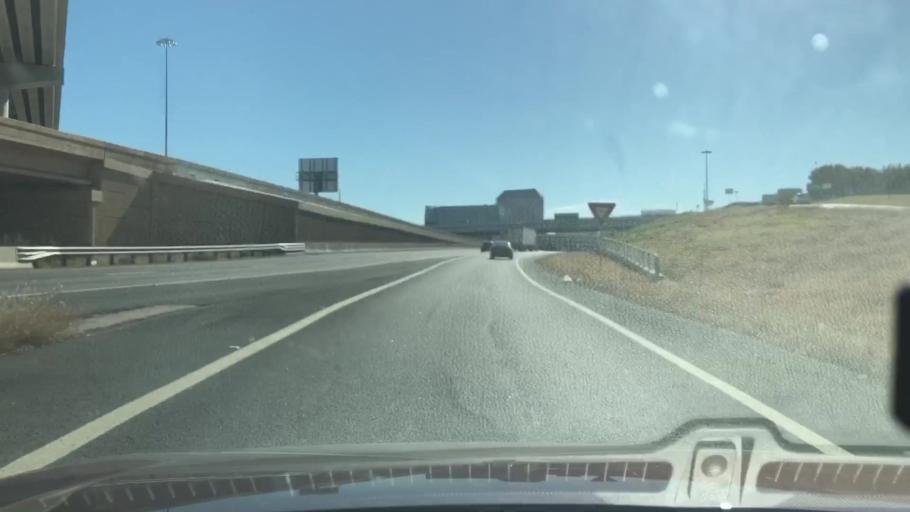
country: US
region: Texas
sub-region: Dallas County
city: Irving
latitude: 32.8813
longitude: -96.9489
